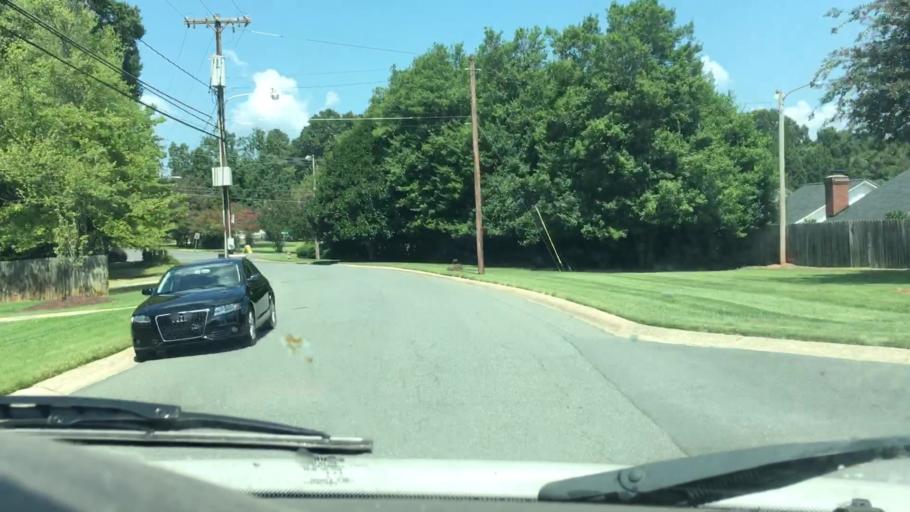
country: US
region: North Carolina
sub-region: Mecklenburg County
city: Cornelius
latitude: 35.4777
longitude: -80.8675
